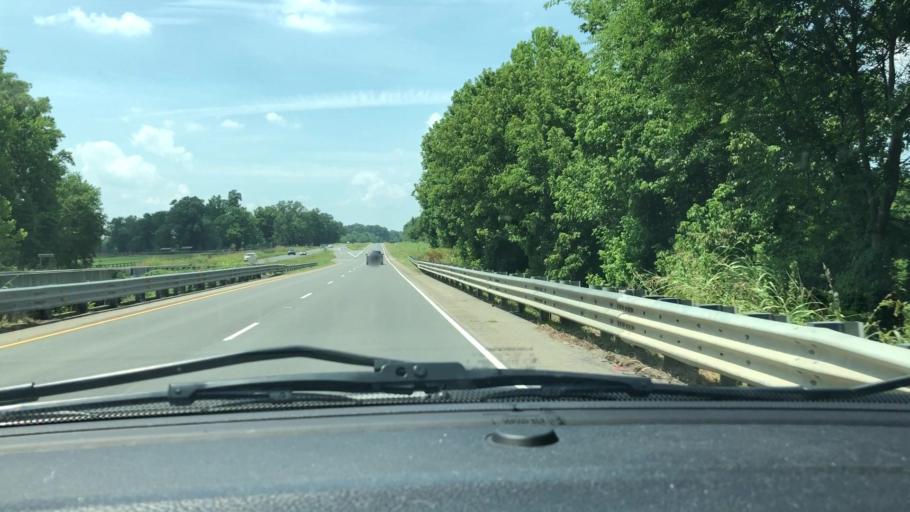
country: US
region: North Carolina
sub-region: Chatham County
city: Siler City
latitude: 35.6599
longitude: -79.4005
